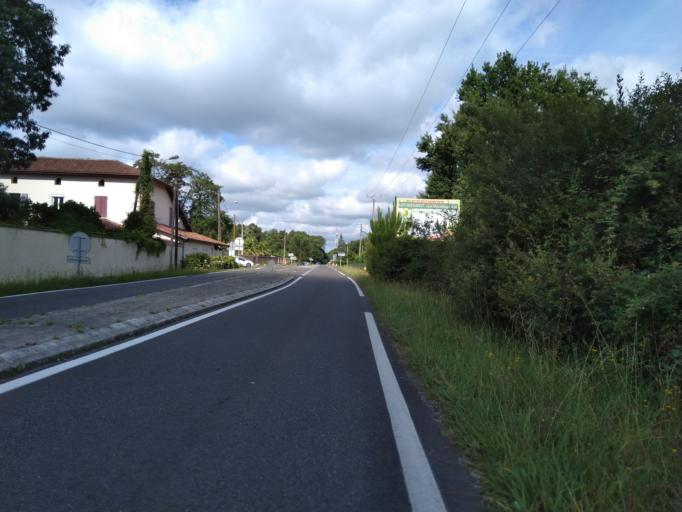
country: FR
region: Aquitaine
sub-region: Departement des Landes
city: Mees
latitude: 43.7317
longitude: -1.0989
